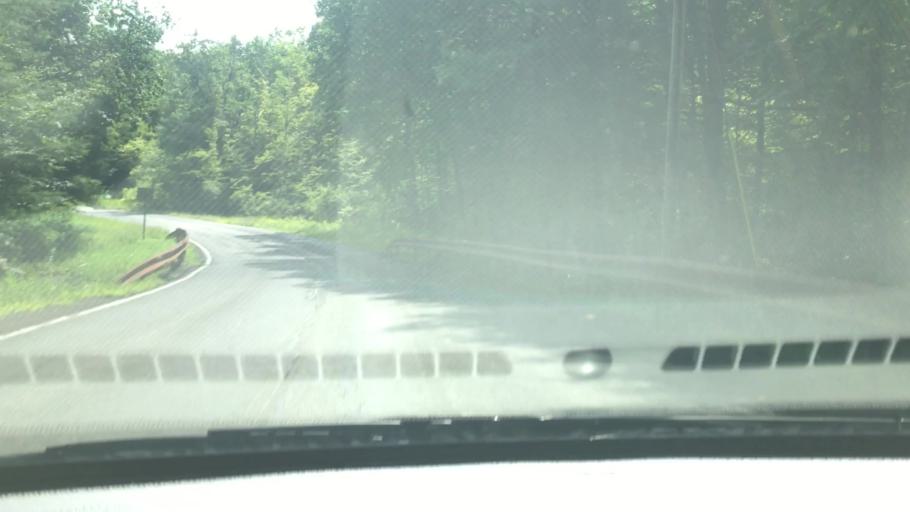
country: US
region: New York
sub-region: Ulster County
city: Shokan
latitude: 41.9298
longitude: -74.2419
